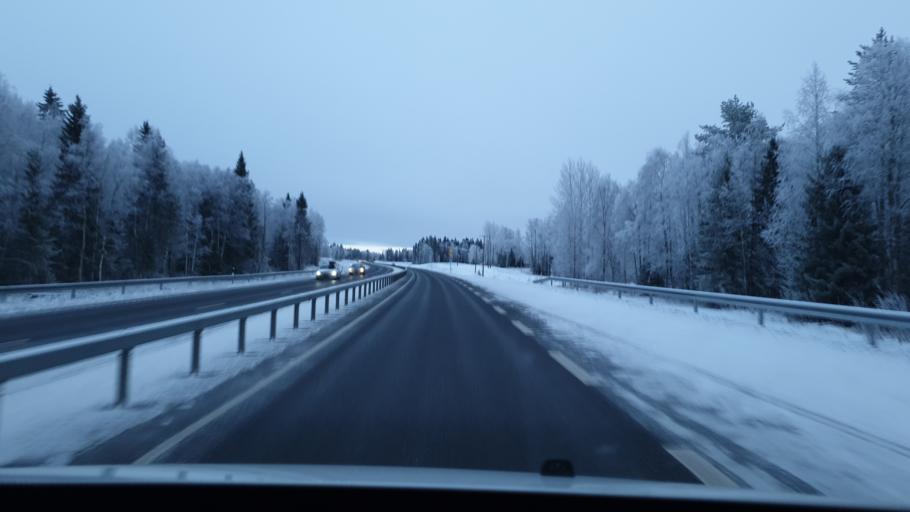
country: FI
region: Lapland
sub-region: Kemi-Tornio
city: Kemi
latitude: 65.6748
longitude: 24.7857
